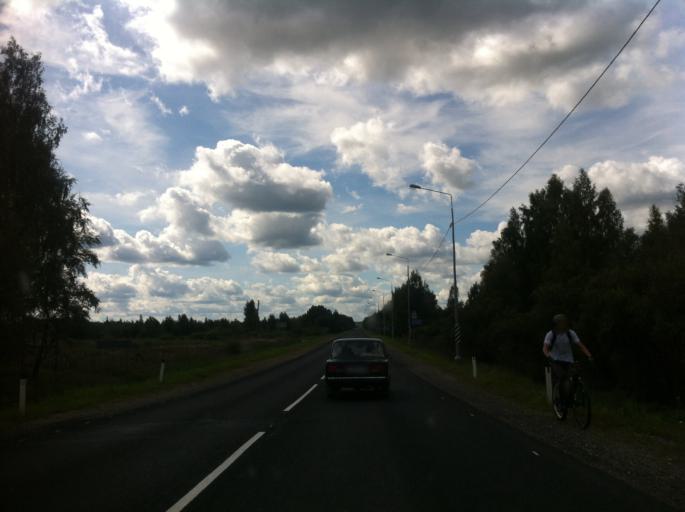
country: RU
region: Pskov
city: Izborsk
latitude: 57.7169
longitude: 27.9200
